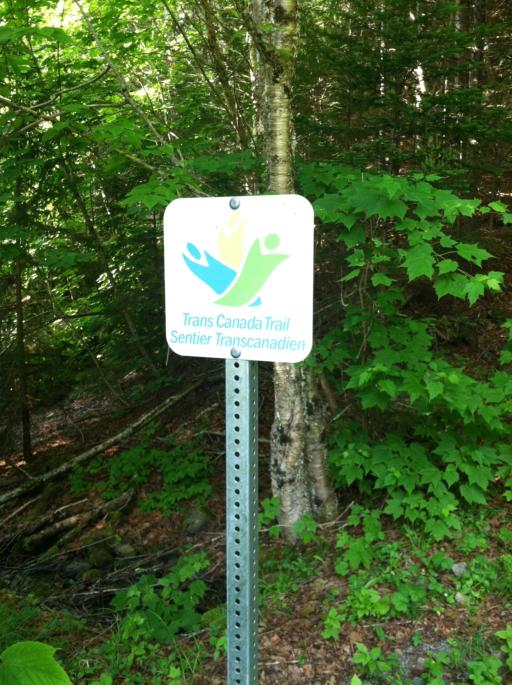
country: CA
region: New Brunswick
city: Salisbury
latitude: 45.6100
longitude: -64.9587
